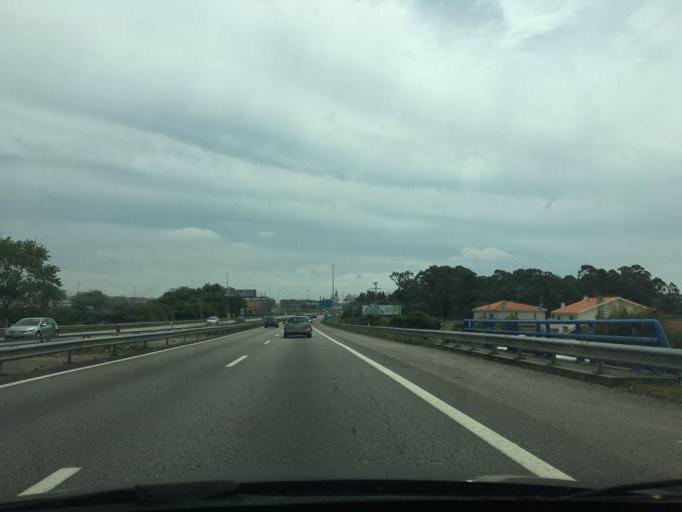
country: PT
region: Porto
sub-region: Matosinhos
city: Santa Cruz do Bispo
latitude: 41.2244
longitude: -8.6938
